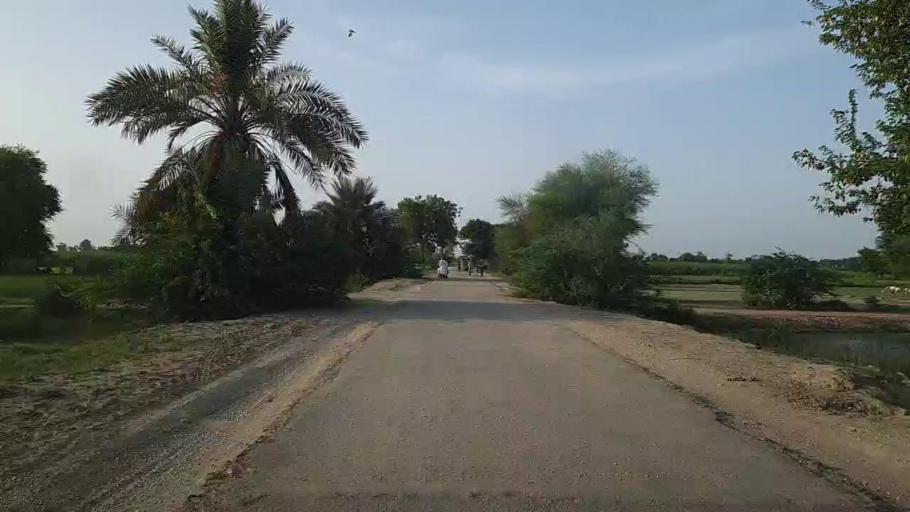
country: PK
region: Sindh
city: Bhiria
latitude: 26.9024
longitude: 68.2631
